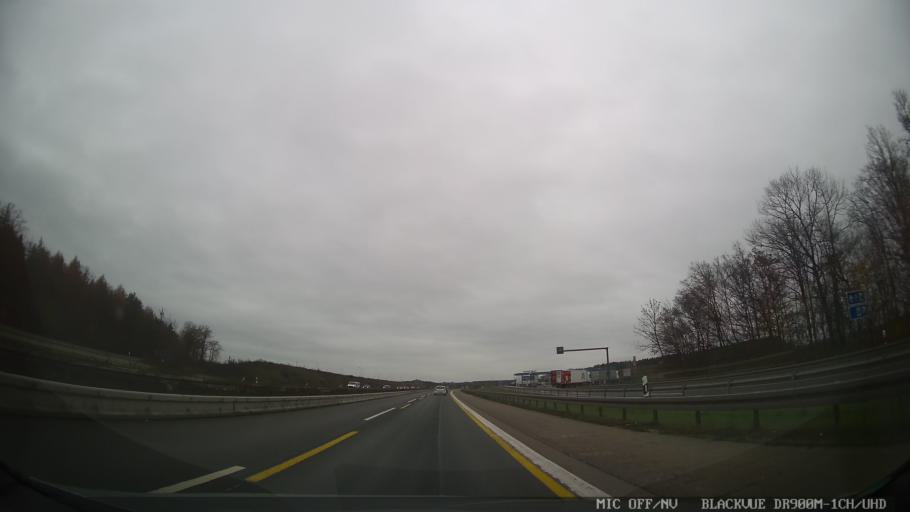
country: DE
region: Bavaria
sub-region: Regierungsbezirk Mittelfranken
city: Herzogenaurach
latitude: 49.5783
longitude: 10.9290
